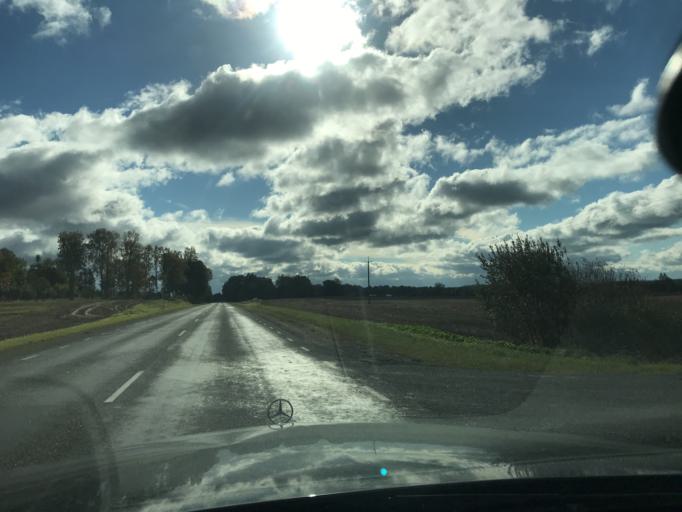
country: EE
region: Vorumaa
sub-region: Antsla vald
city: Vana-Antsla
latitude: 57.9671
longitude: 26.2654
